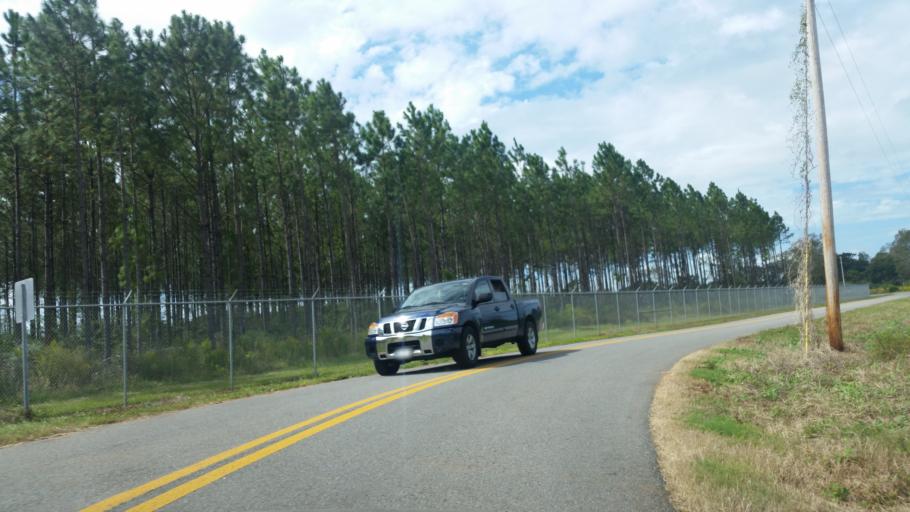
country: US
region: Florida
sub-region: Santa Rosa County
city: Point Baker
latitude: 30.7368
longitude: -87.0312
